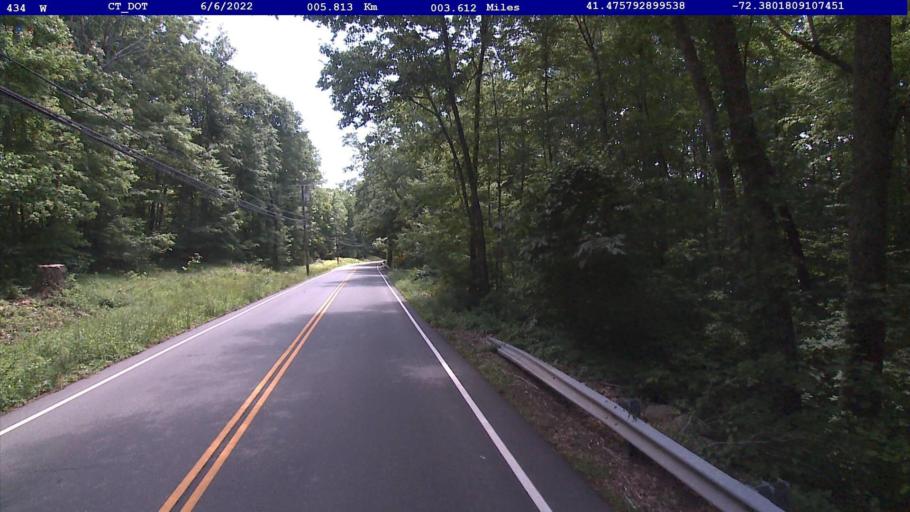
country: US
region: Connecticut
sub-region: Middlesex County
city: Moodus
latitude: 41.4757
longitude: -72.3800
